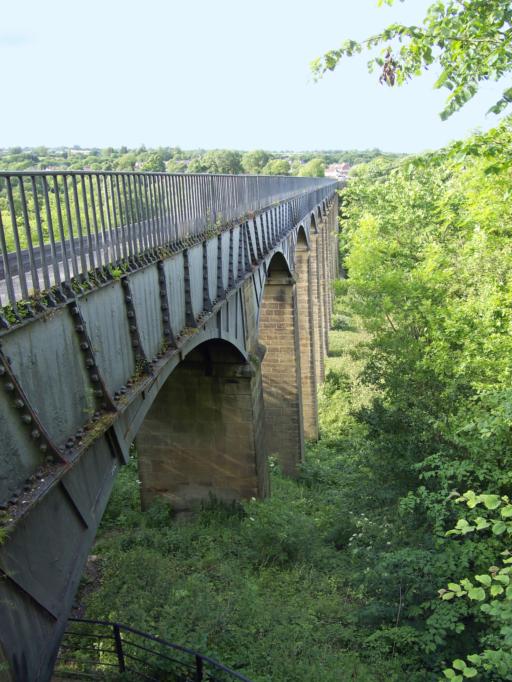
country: GB
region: Wales
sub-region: Wrexham
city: Chirk
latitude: 52.9689
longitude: -3.0881
